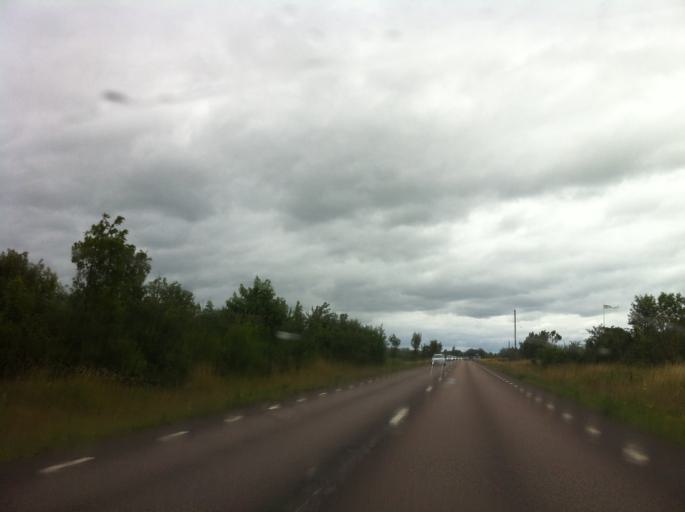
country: SE
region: Kalmar
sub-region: Borgholms Kommun
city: Borgholm
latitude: 57.1131
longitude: 16.9535
